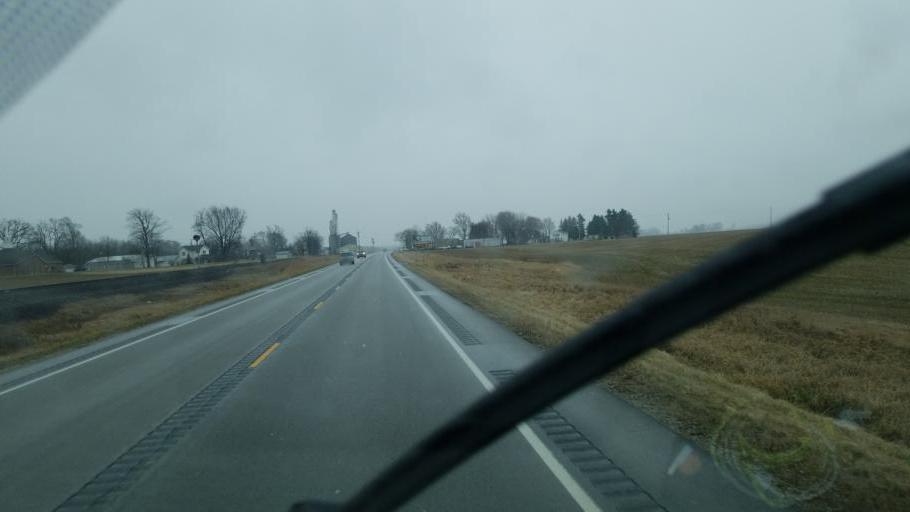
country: US
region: Indiana
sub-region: Wabash County
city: Mount Vernon
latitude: 40.7286
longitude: -85.7852
